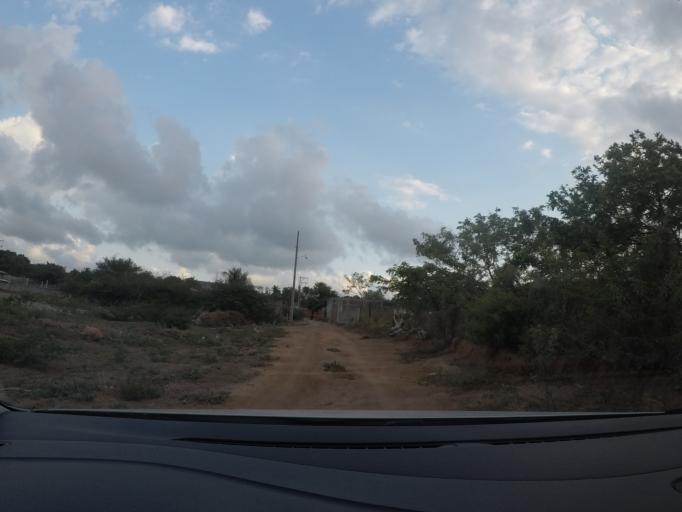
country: MX
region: Oaxaca
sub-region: Salina Cruz
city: Salina Cruz
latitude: 16.2062
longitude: -95.2020
